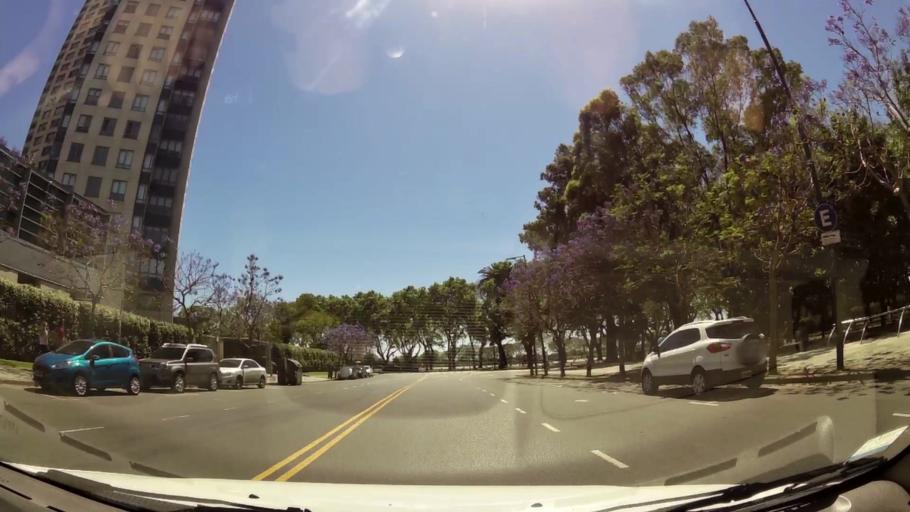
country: AR
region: Buenos Aires F.D.
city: Buenos Aires
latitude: -34.6130
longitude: -58.3595
